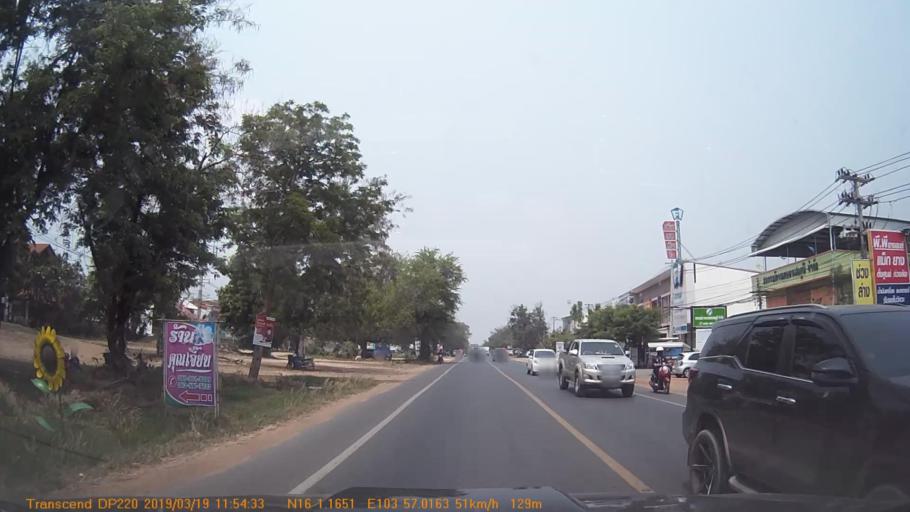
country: TH
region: Roi Et
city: Ban Selaphum
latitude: 16.0195
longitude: 103.9502
